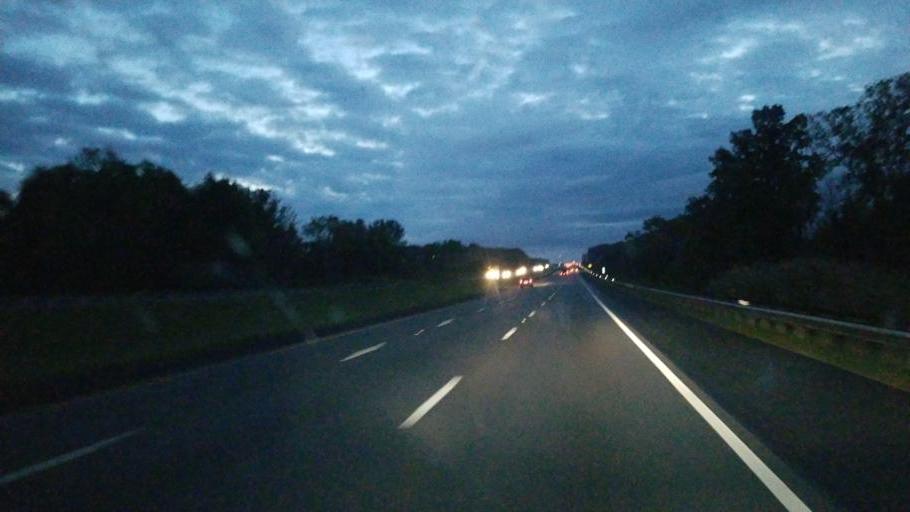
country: US
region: Ohio
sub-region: Medina County
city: Westfield Center
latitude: 41.0040
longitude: -81.9587
